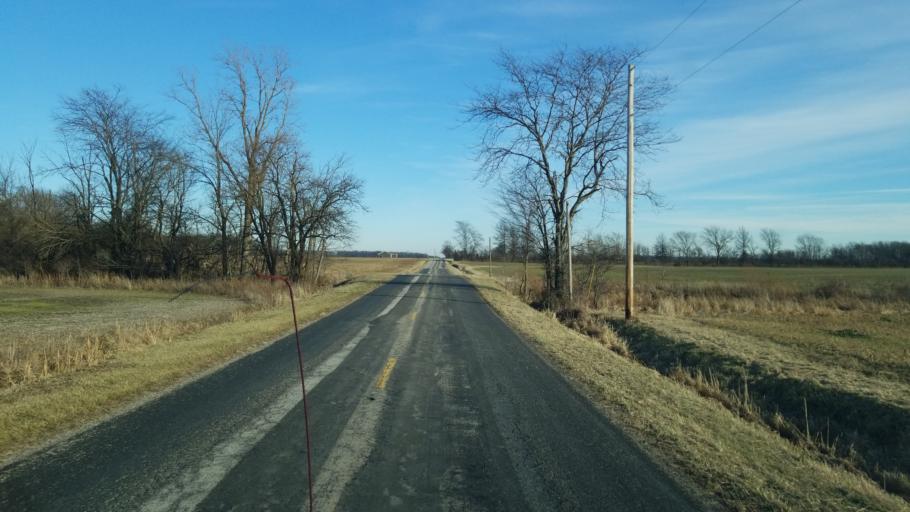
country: US
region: Ohio
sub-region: Huron County
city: Bellevue
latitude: 41.1802
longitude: -82.8261
